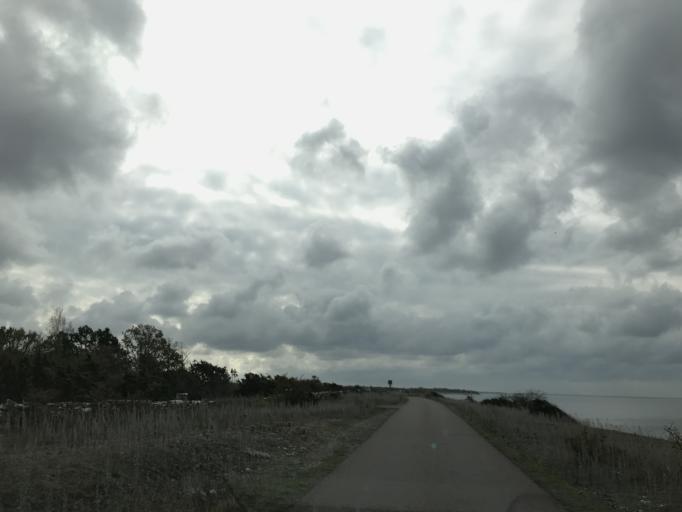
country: SE
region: Kalmar
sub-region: Borgholms Kommun
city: Borgholm
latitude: 57.0570
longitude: 16.8375
